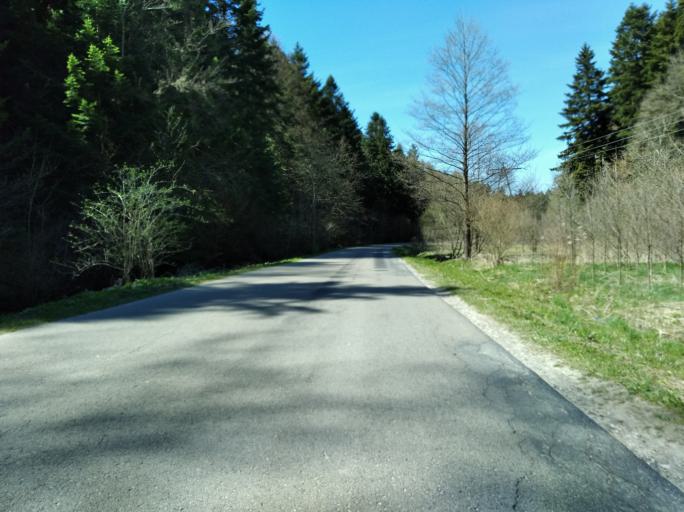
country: PL
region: Subcarpathian Voivodeship
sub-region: Powiat brzozowski
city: Golcowa
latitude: 49.7487
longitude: 22.0722
